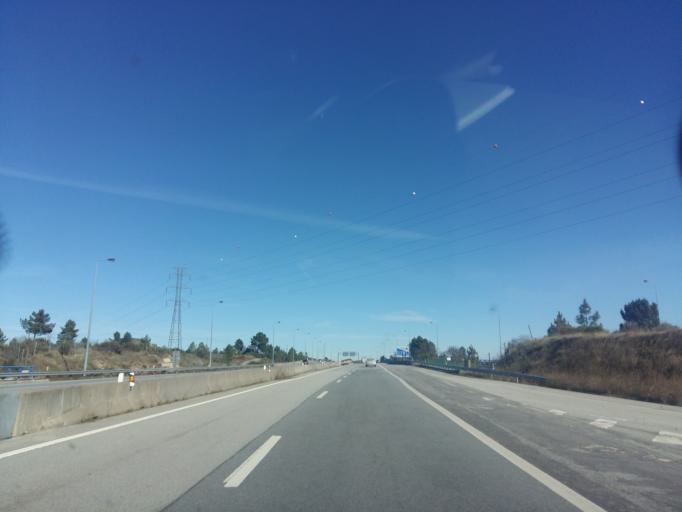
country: PT
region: Guarda
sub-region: Guarda
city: Sequeira
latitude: 40.5694
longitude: -7.2146
